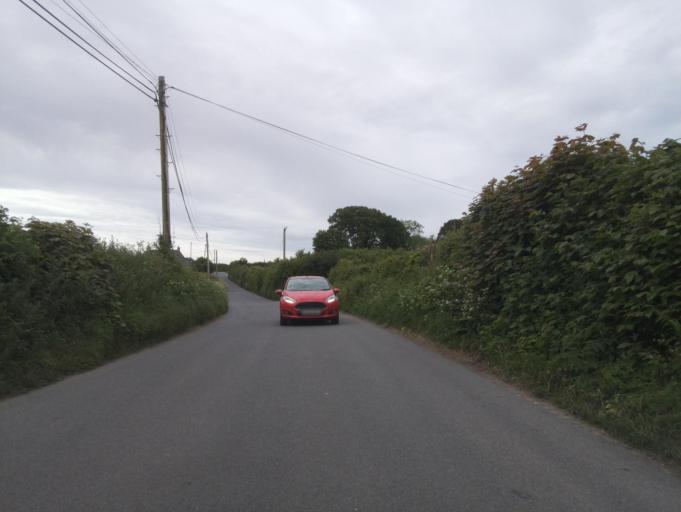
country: GB
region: England
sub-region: Devon
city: Dartmouth
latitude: 50.3470
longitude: -3.6576
